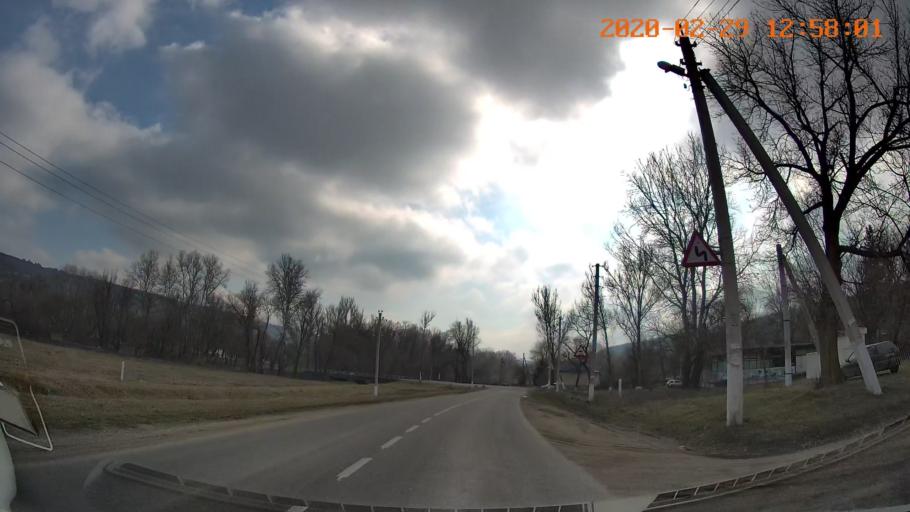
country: MD
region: Telenesti
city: Camenca
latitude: 48.0722
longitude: 28.7177
